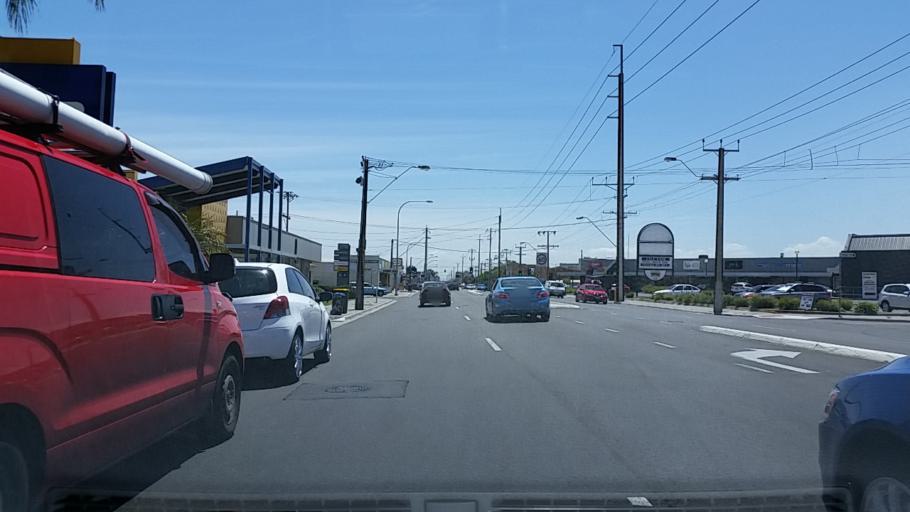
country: AU
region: South Australia
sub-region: Charles Sturt
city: Findon
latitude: -34.8940
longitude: 138.5317
